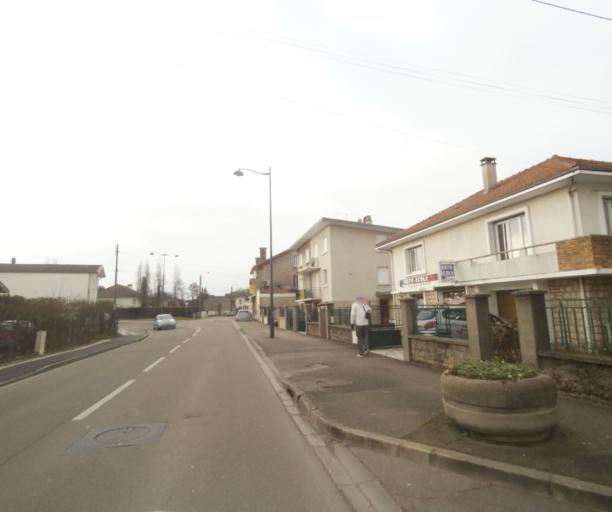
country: FR
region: Champagne-Ardenne
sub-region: Departement de la Haute-Marne
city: Bettancourt-la-Ferree
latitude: 48.6411
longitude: 4.9613
